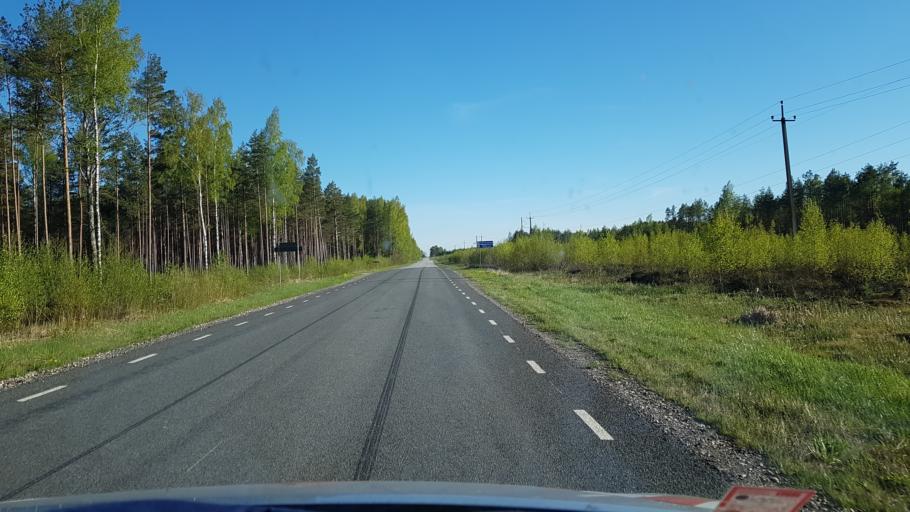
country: EE
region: Vorumaa
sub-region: Voru linn
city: Voru
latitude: 57.9378
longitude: 26.9528
